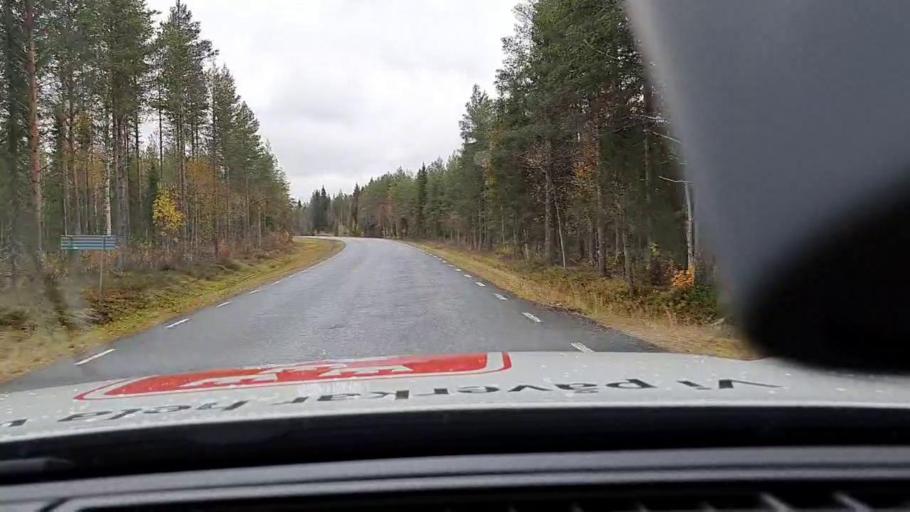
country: SE
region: Norrbotten
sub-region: Haparanda Kommun
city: Haparanda
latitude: 65.9024
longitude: 23.8334
